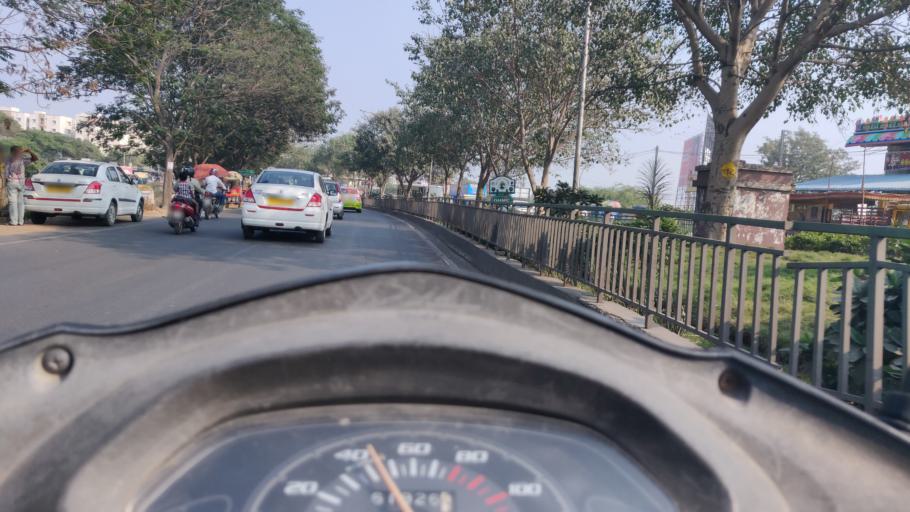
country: IN
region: Telangana
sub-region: Rangareddi
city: Uppal Kalan
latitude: 17.4013
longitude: 78.5801
